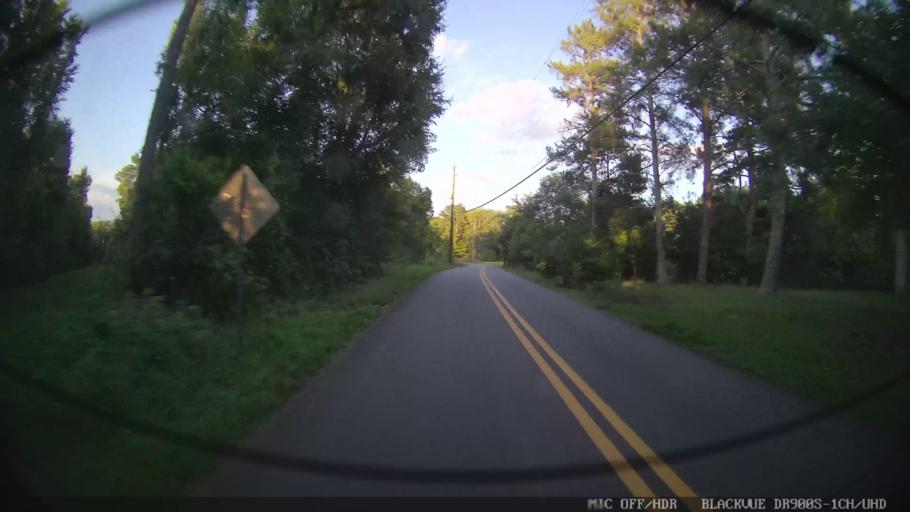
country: US
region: Georgia
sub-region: Bartow County
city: Emerson
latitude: 34.1023
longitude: -84.7177
